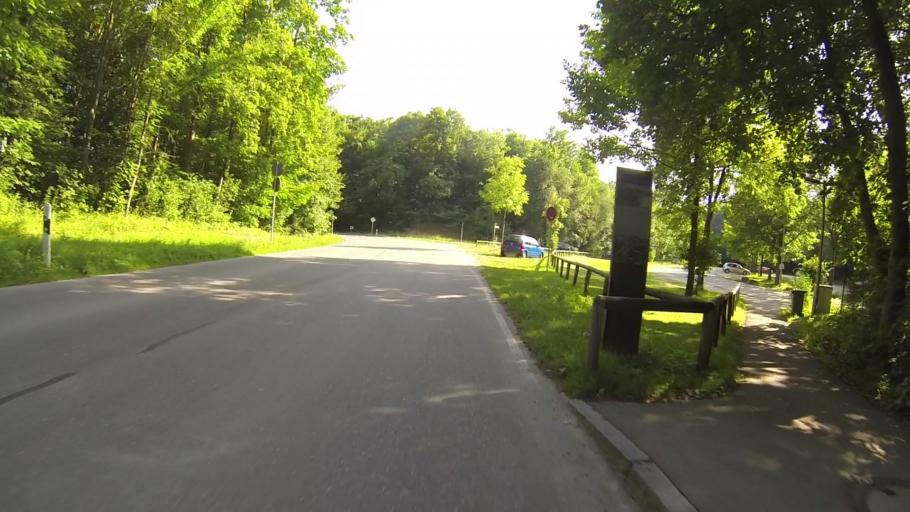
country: DE
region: Bavaria
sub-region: Swabia
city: Neu-Ulm
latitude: 48.4190
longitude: 10.0247
